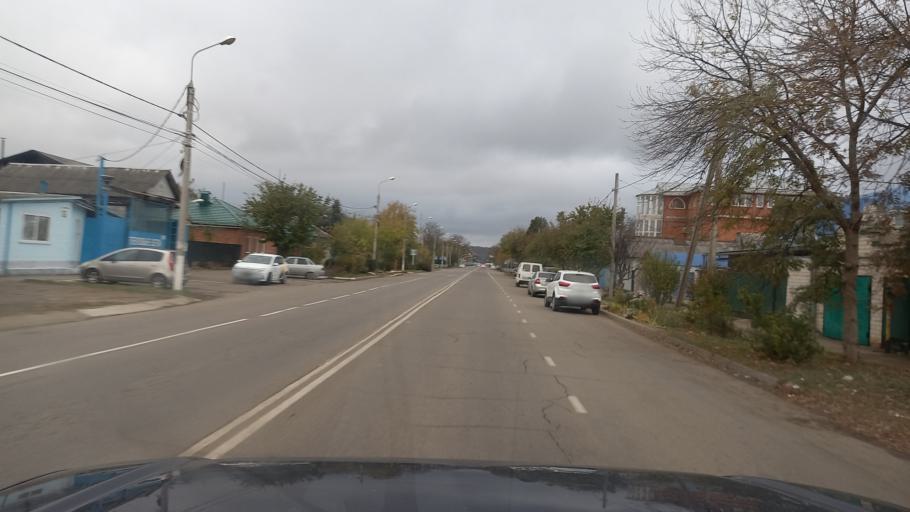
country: RU
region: Adygeya
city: Maykop
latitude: 44.6149
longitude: 40.1134
